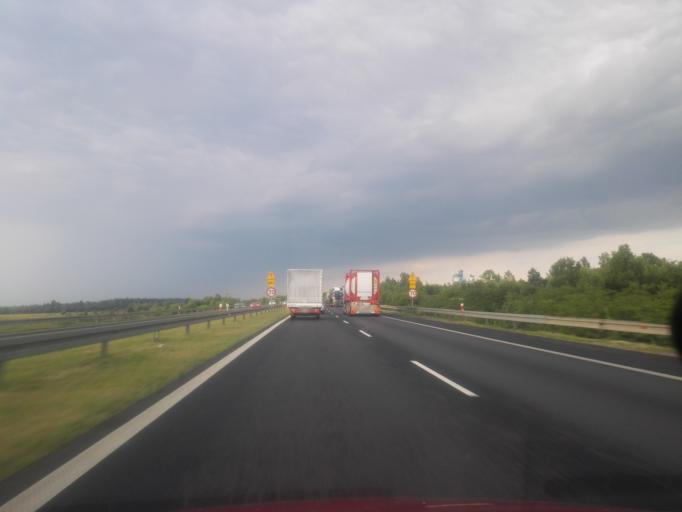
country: PL
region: Silesian Voivodeship
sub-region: Powiat czestochowski
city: Koscielec
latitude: 50.8845
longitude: 19.1704
